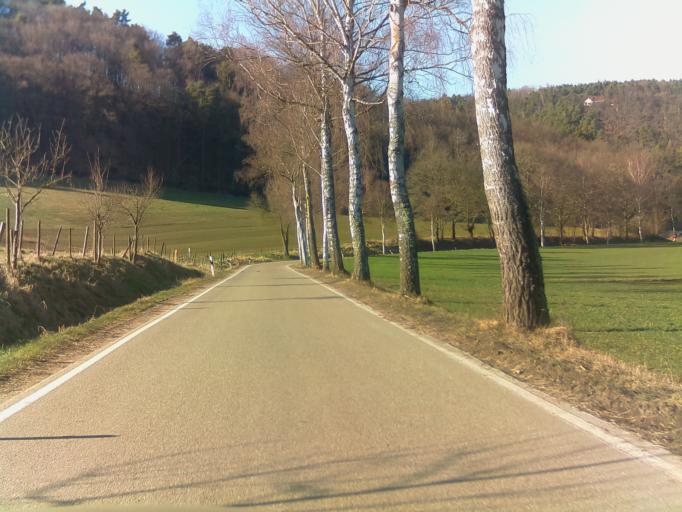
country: DE
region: Rheinland-Pfalz
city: Altleiningen
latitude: 49.5079
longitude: 8.0959
